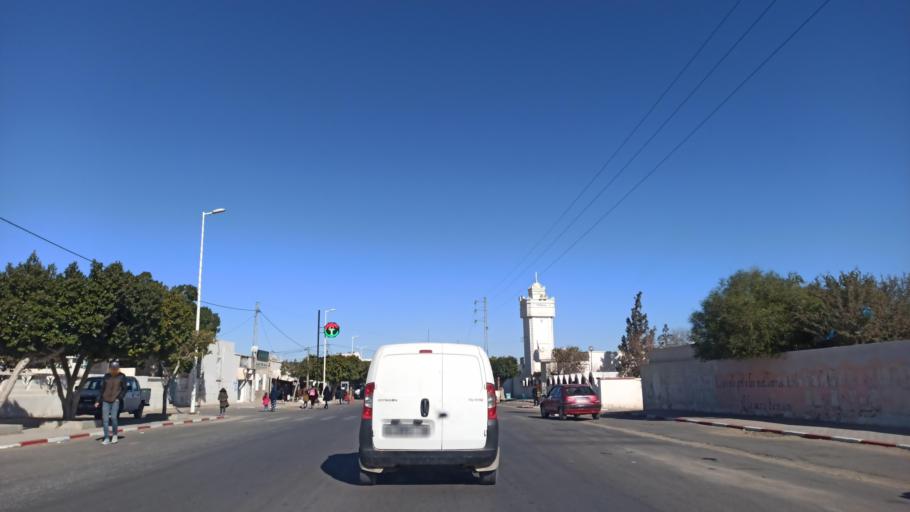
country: TN
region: Sidi Bu Zayd
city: Bi'r al Hufayy
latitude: 34.9292
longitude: 9.1936
